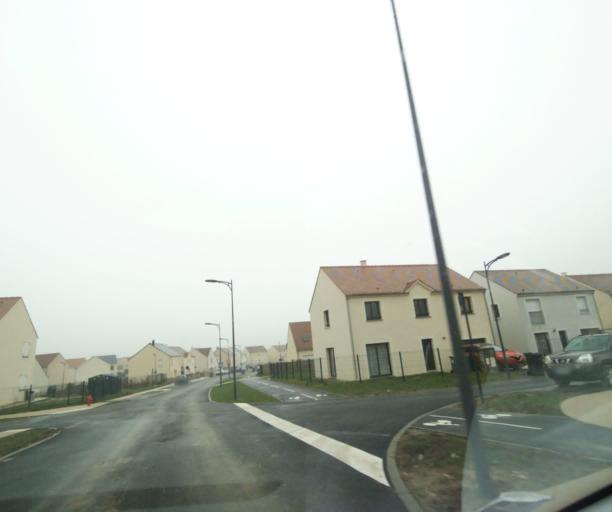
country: FR
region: Ile-de-France
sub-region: Departement de Seine-et-Marne
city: Dammartin-en-Goele
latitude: 49.0616
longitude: 2.6709
